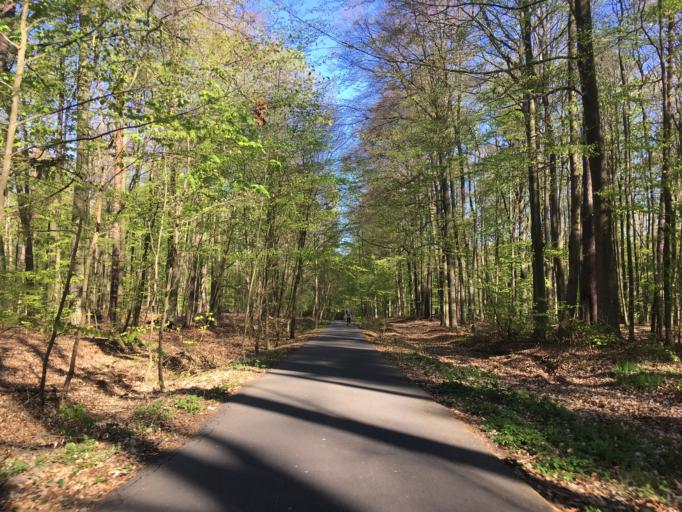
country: DE
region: Brandenburg
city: Wandlitz
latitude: 52.7258
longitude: 13.5123
